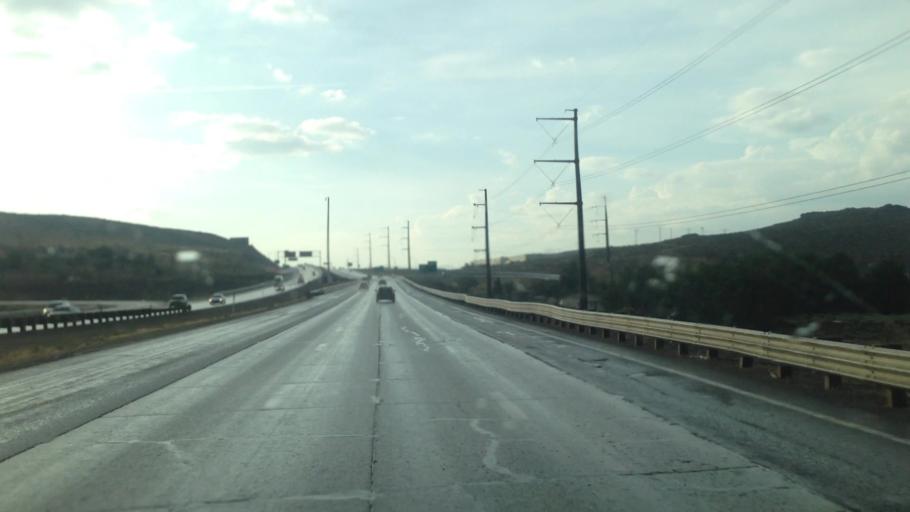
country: US
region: Nevada
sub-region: Washoe County
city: Golden Valley
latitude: 39.5874
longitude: -119.8241
